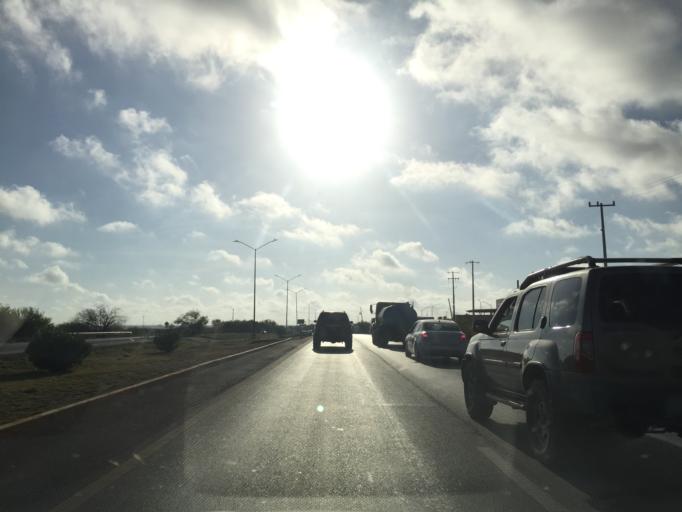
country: MX
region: Tamaulipas
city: Nuevo Laredo
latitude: 27.4265
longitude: -99.5204
